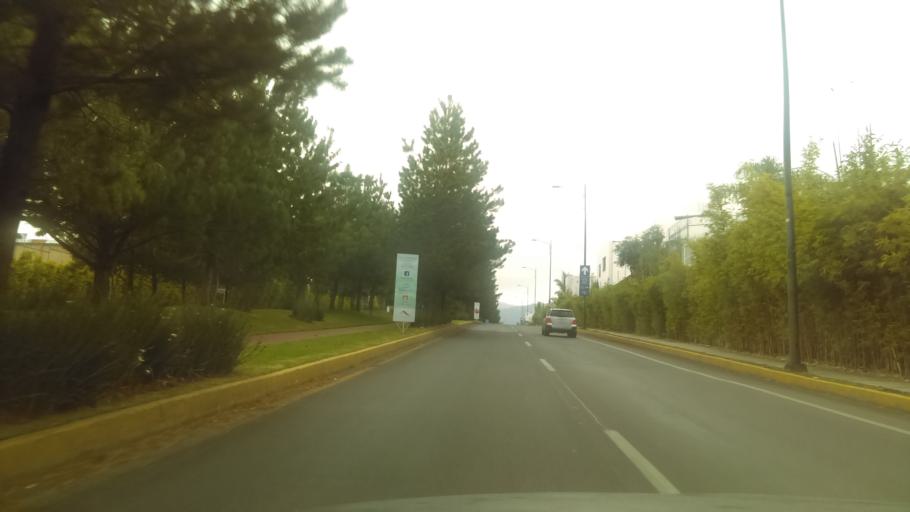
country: MX
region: Michoacan
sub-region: Morelia
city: Montana Monarca (Punta Altozano)
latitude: 19.6619
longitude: -101.1645
